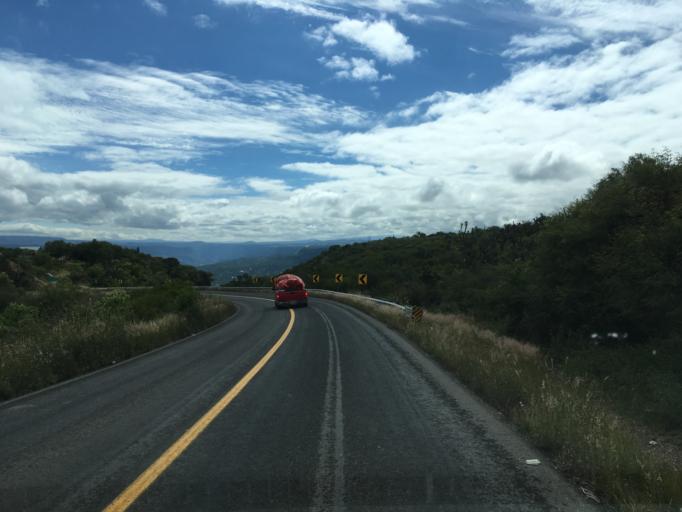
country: MX
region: Hidalgo
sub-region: Atotonilco el Grande
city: Santa Maria Amajac
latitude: 20.4096
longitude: -98.6969
